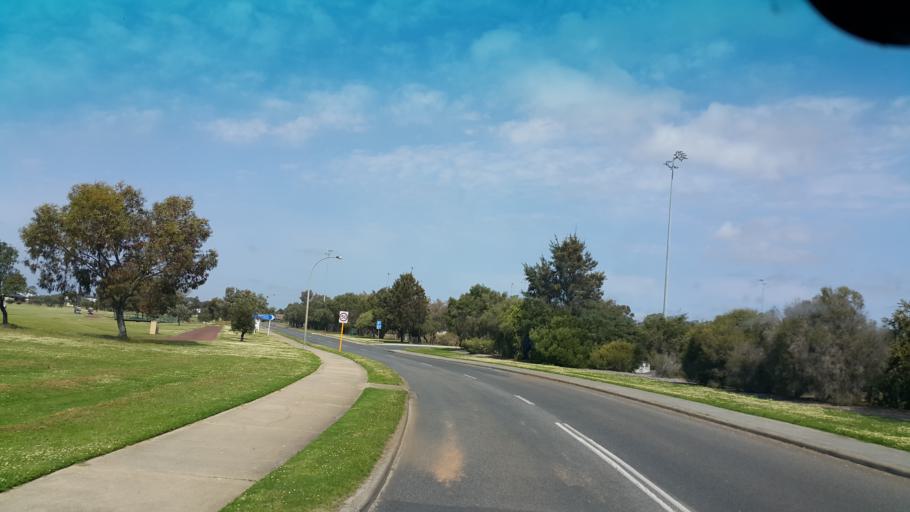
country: AU
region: Western Australia
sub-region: Busselton
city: Dunsborough
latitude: -33.6187
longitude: 115.1073
